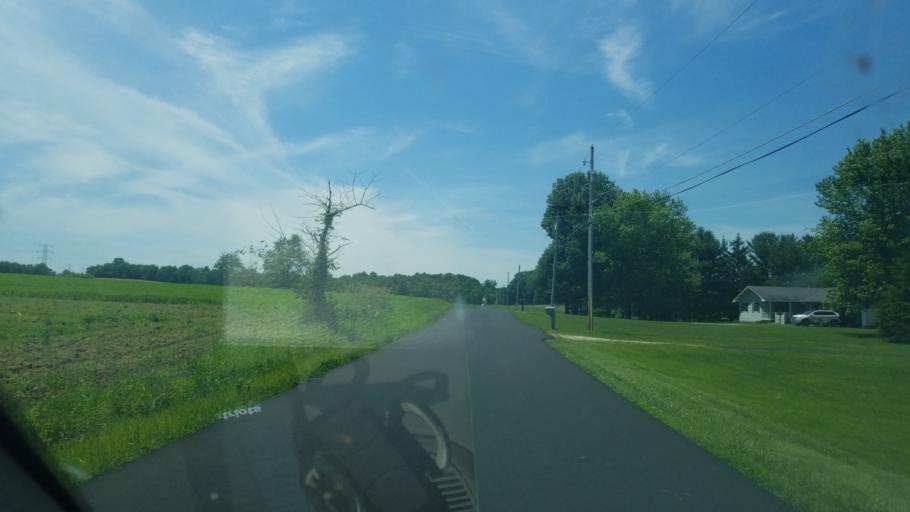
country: US
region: Ohio
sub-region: Stark County
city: Alliance
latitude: 40.8579
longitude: -81.1514
